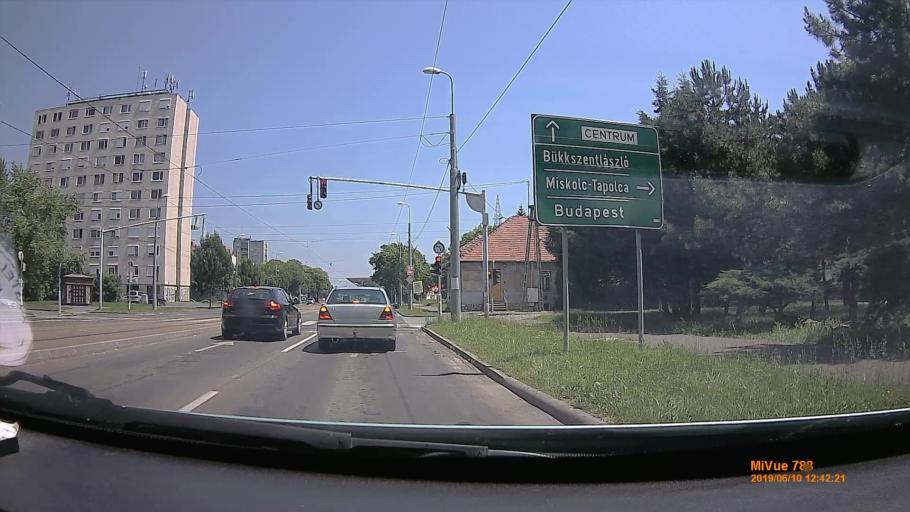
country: HU
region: Borsod-Abauj-Zemplen
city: Saly
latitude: 48.0508
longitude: 20.5557
